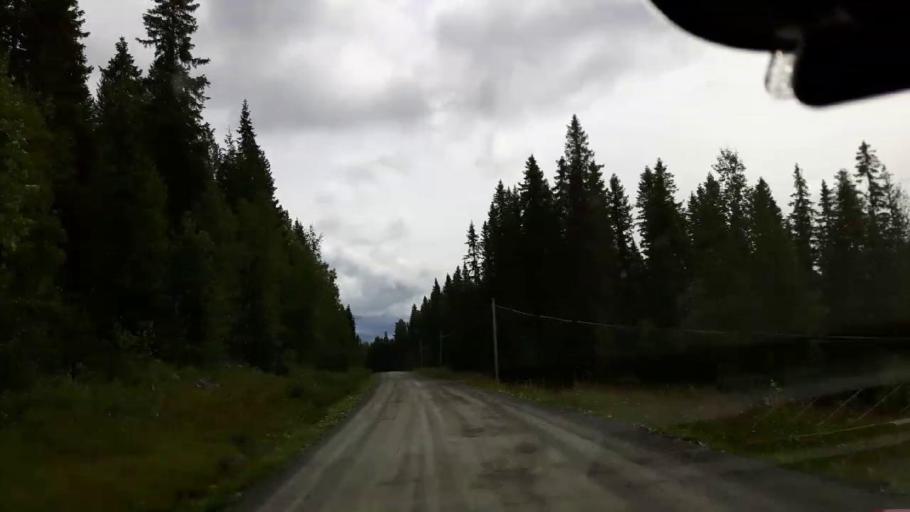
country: SE
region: Jaemtland
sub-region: Krokoms Kommun
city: Valla
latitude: 63.6762
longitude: 13.9350
